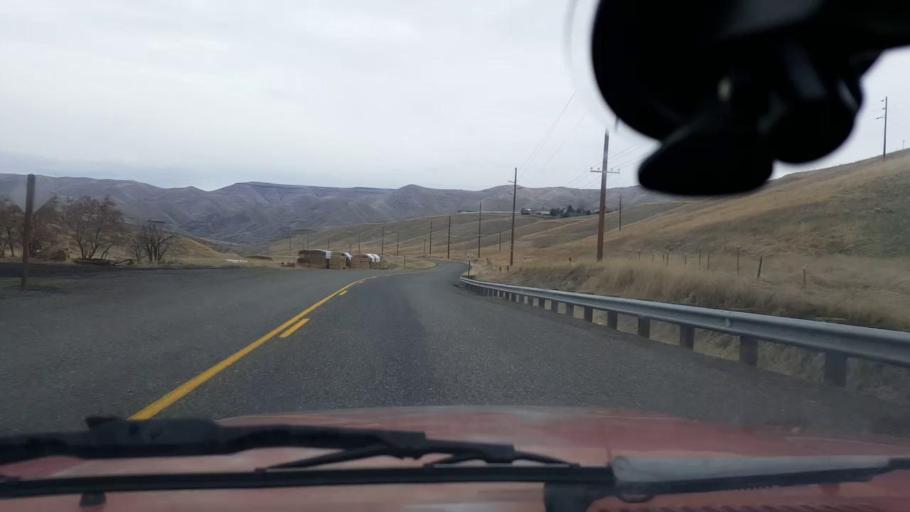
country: US
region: Washington
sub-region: Asotin County
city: Clarkston Heights-Vineland
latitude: 46.4007
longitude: -117.1011
